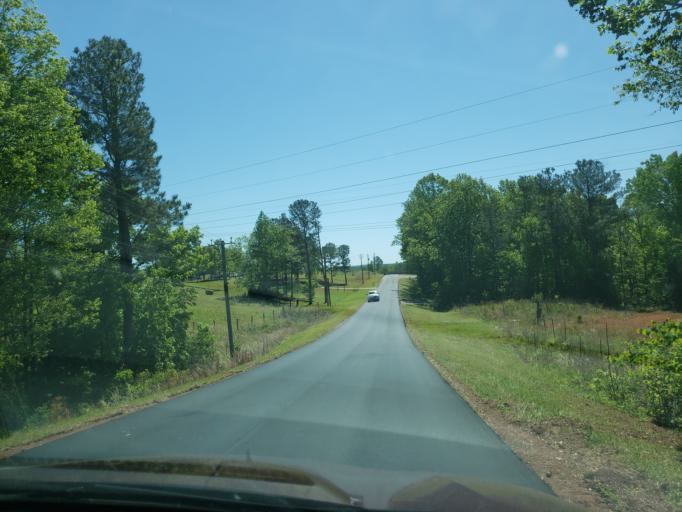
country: US
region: Alabama
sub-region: Tallapoosa County
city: Dadeville
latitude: 32.7022
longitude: -85.8704
